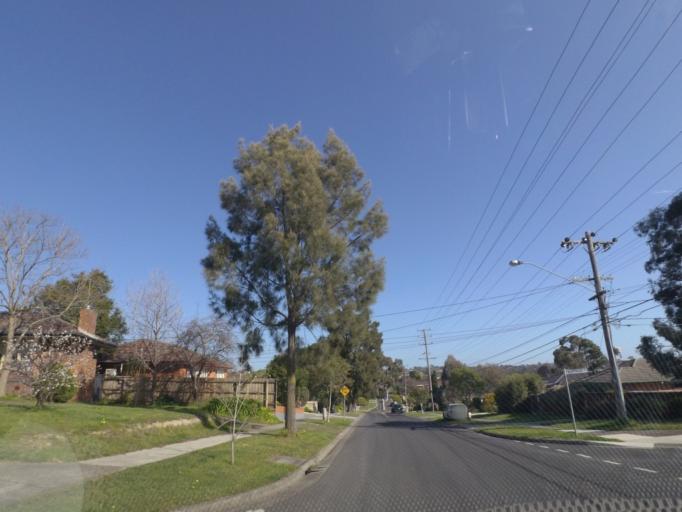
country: AU
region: Victoria
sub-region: Boroondara
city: Balwyn North
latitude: -37.7800
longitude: 145.1036
